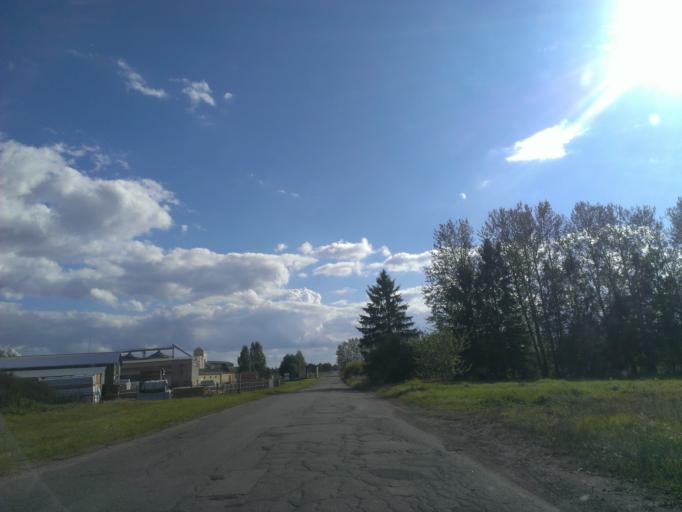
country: LV
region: Sigulda
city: Sigulda
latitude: 57.1446
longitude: 24.8926
